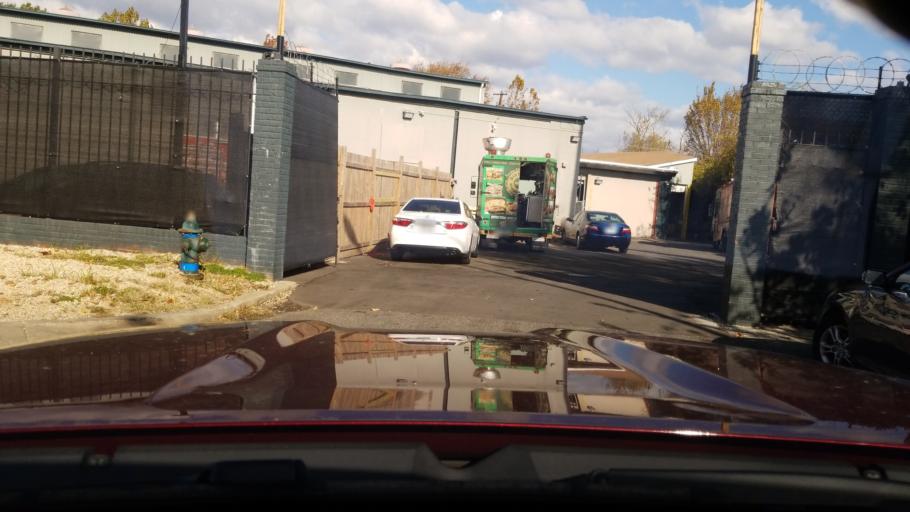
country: US
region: Maryland
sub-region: Prince George's County
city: Hillcrest Heights
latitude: 38.8693
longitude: -76.9851
